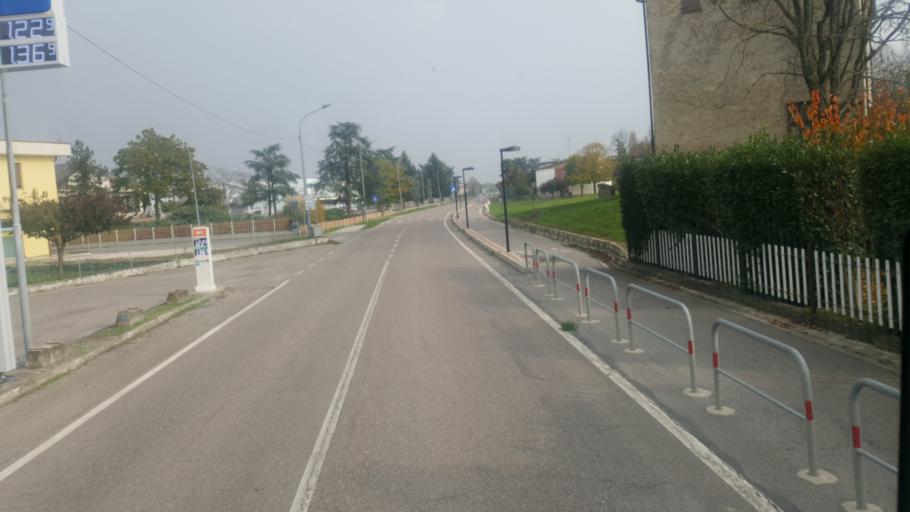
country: IT
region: Lombardy
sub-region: Provincia di Mantova
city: Sermide
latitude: 44.9471
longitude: 11.2864
